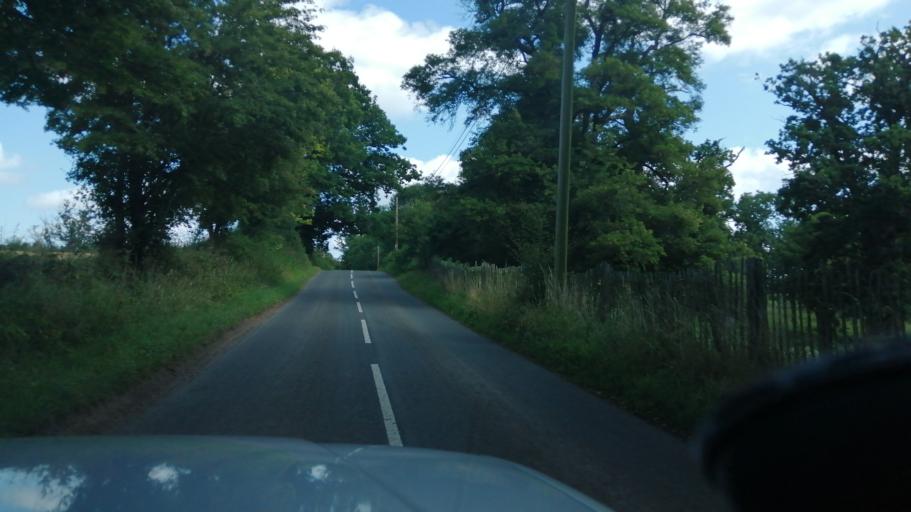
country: GB
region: England
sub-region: Herefordshire
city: Moccas
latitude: 52.0830
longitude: -2.9642
